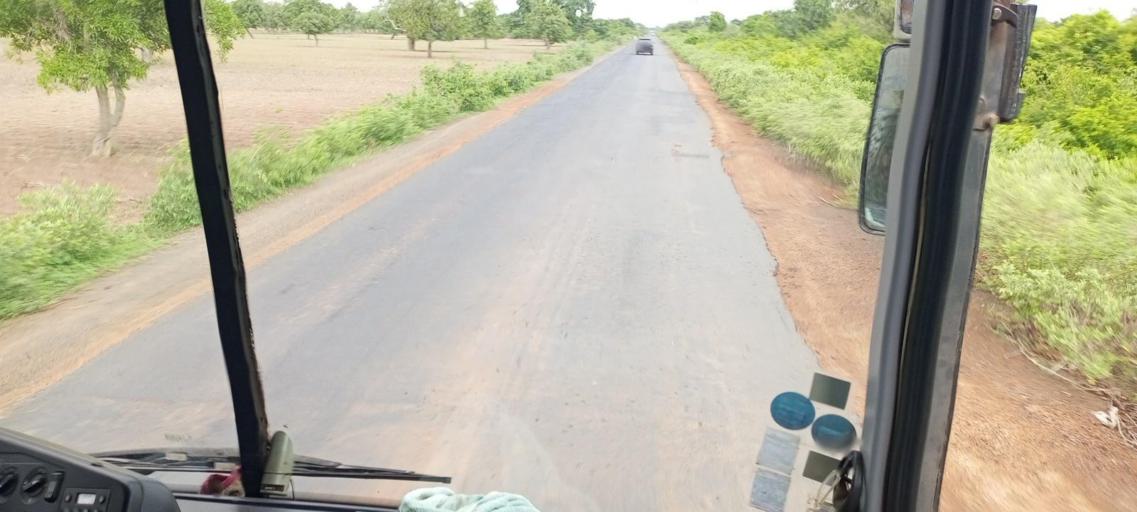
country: ML
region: Segou
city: Bla
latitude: 12.7697
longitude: -5.7424
